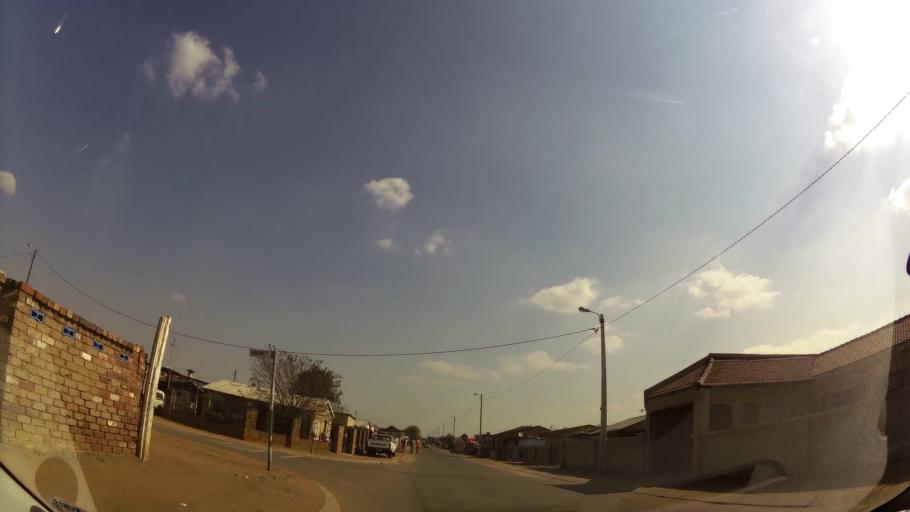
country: ZA
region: Gauteng
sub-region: Ekurhuleni Metropolitan Municipality
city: Brakpan
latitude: -26.1498
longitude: 28.4088
